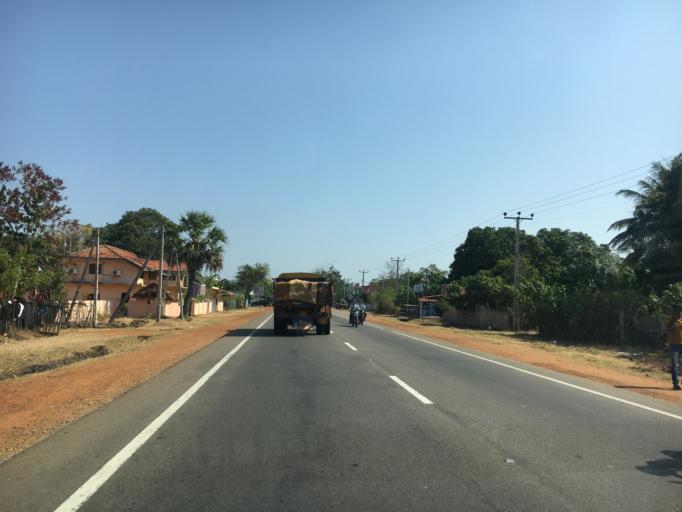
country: LK
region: Northern Province
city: Kilinochchi
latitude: 9.4330
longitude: 80.4077
